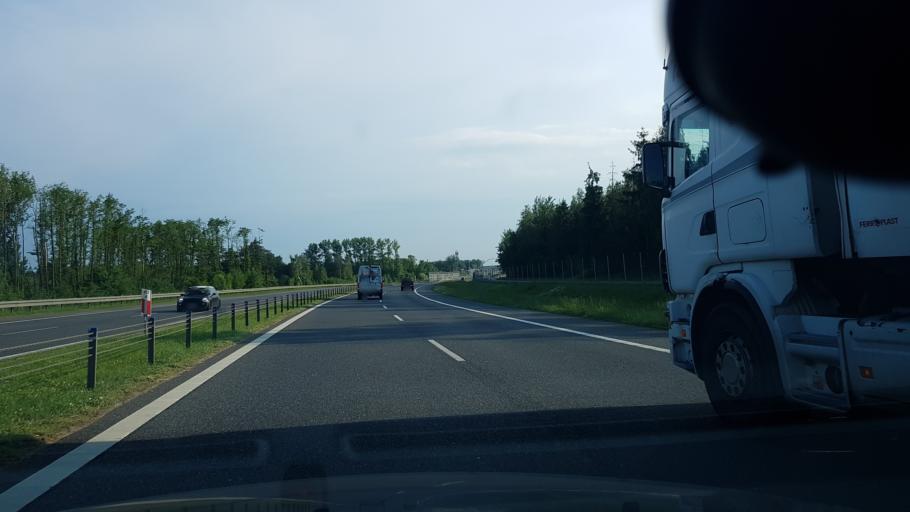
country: PL
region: Masovian Voivodeship
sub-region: Powiat zyrardowski
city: Mszczonow
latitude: 51.9605
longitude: 20.4986
